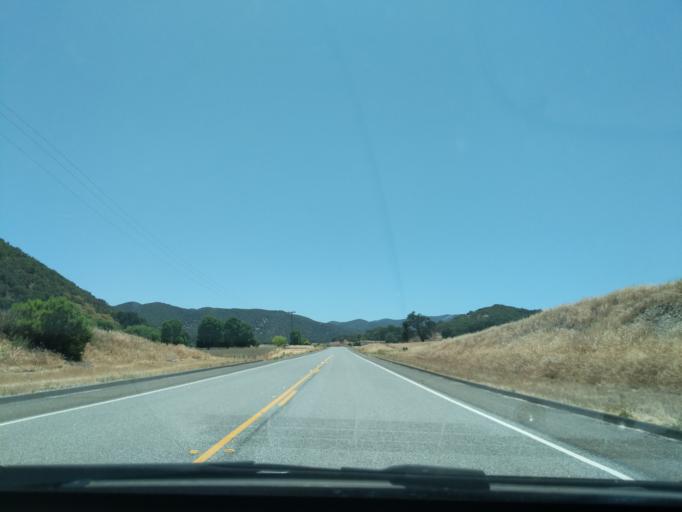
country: US
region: California
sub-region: Monterey County
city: King City
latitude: 36.1098
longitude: -121.1323
